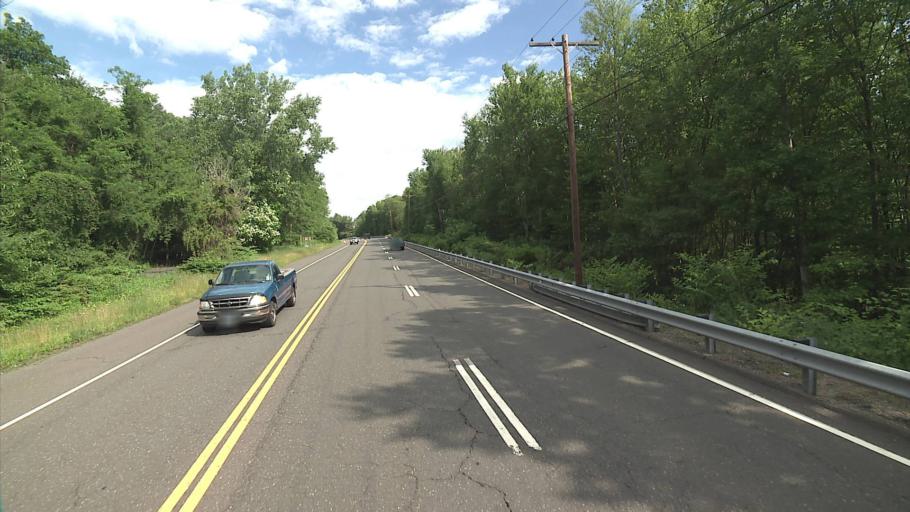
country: US
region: Connecticut
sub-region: New Haven County
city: Naugatuck
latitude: 41.5116
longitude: -73.0643
